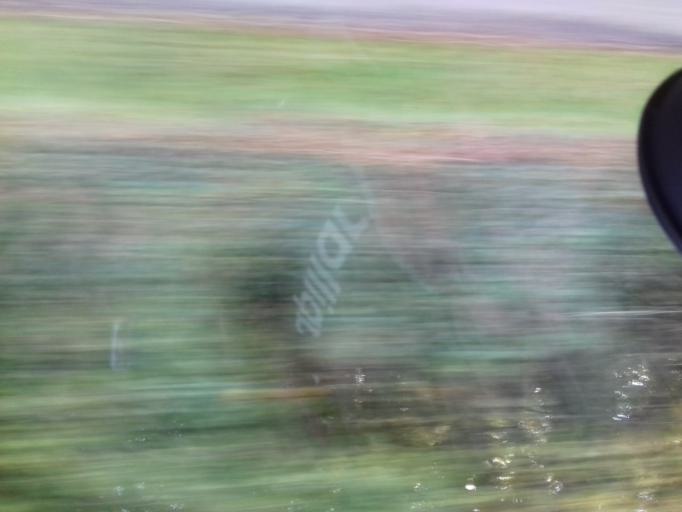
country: IE
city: Kentstown
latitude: 53.6291
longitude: -6.4912
